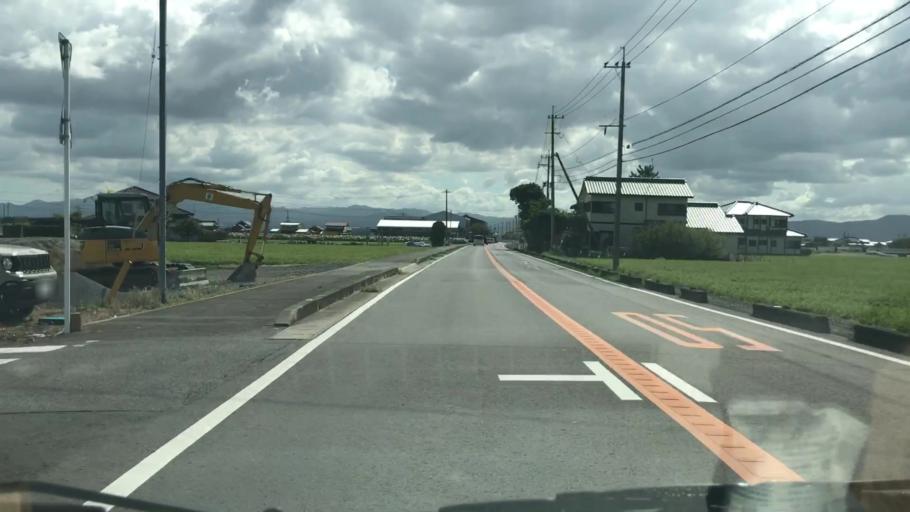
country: JP
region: Saga Prefecture
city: Kashima
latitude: 33.1799
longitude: 130.1880
